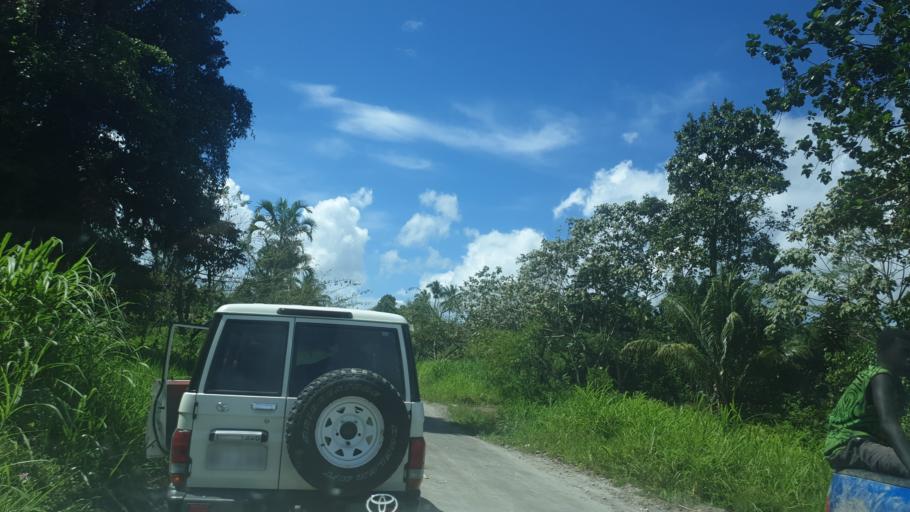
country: PG
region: Bougainville
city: Panguna
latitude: -6.6618
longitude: 155.4556
